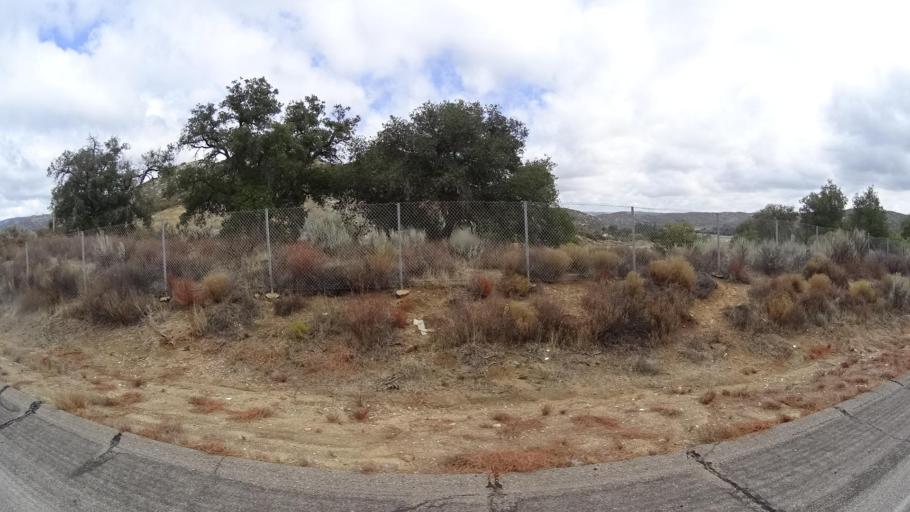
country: US
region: California
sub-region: San Diego County
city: Campo
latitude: 32.7202
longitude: -116.4755
